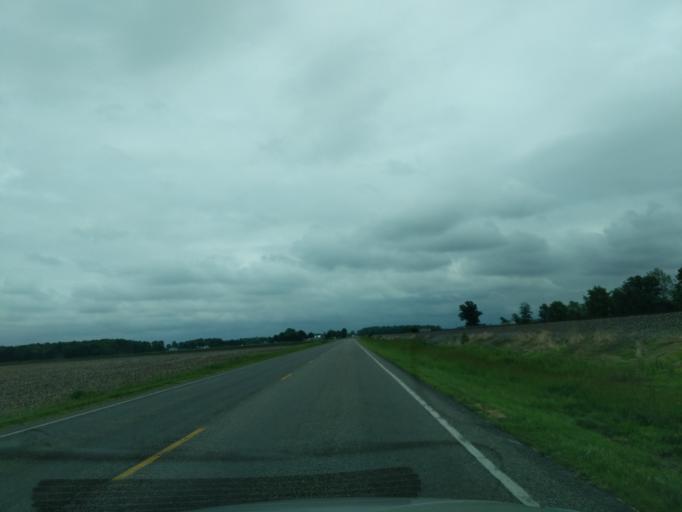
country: US
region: Indiana
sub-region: Madison County
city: Elwood
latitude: 40.2782
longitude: -85.8926
